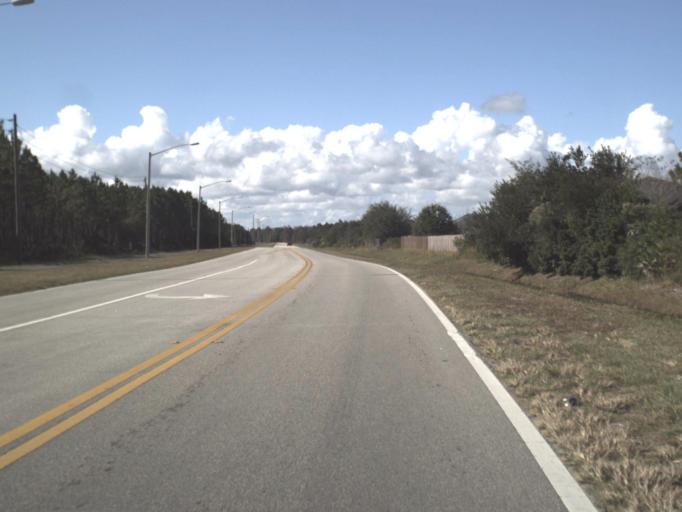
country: US
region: Florida
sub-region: Flagler County
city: Palm Coast
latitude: 29.6020
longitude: -81.2658
